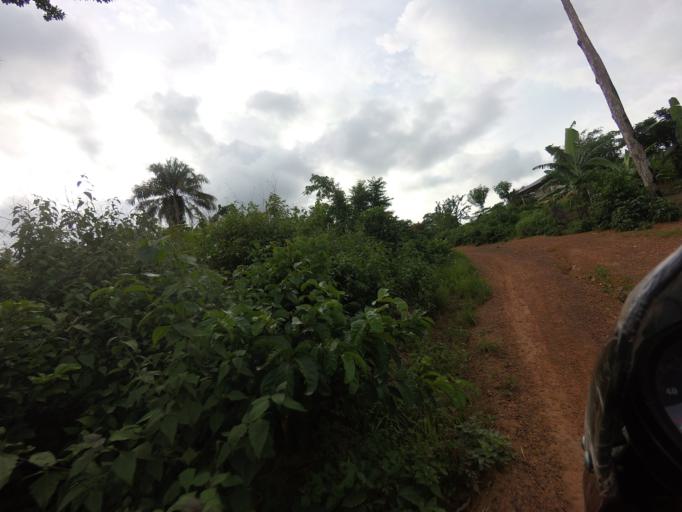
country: SL
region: Eastern Province
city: Jojoima
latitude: 7.7905
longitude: -10.8100
